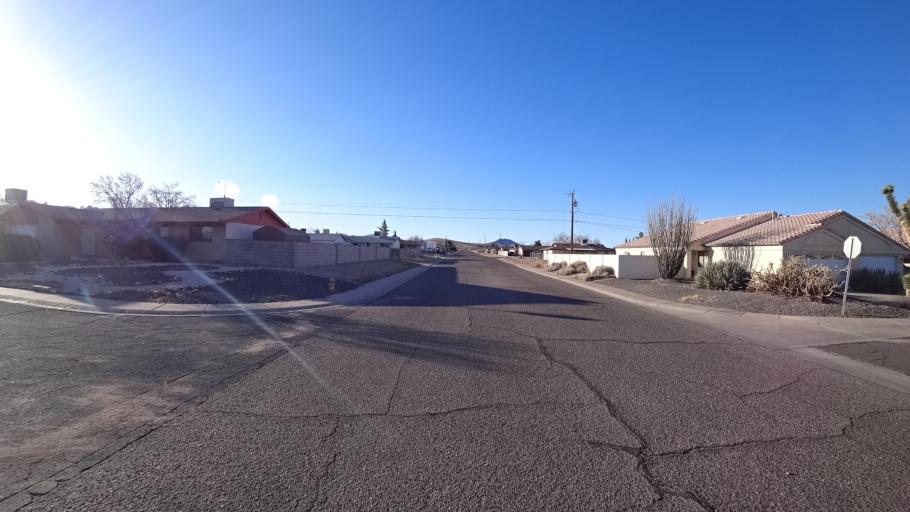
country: US
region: Arizona
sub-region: Mohave County
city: Kingman
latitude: 35.1948
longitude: -114.0136
